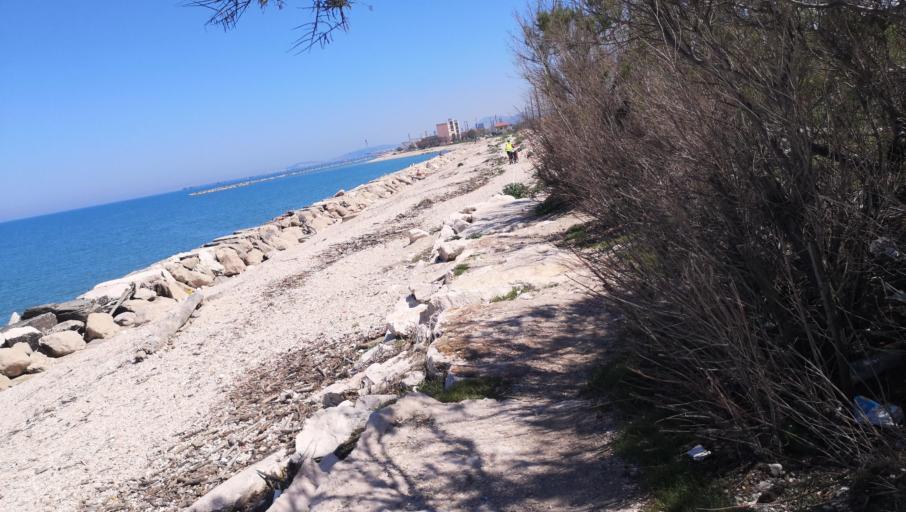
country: IT
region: The Marches
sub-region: Provincia di Ancona
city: Marina di Montemarciano
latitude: 43.6497
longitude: 13.3507
